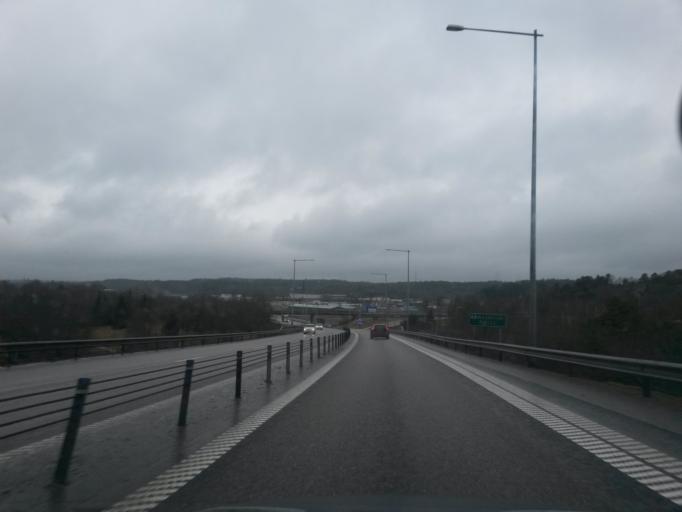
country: SE
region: Vaestra Goetaland
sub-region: Uddevalla Kommun
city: Uddevalla
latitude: 58.3467
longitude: 11.9869
